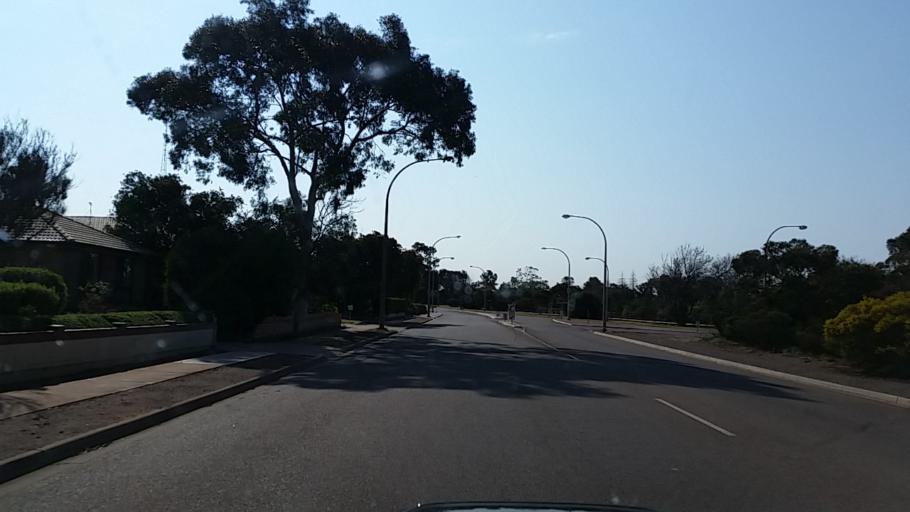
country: AU
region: South Australia
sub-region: Whyalla
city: Whyalla
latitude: -33.0308
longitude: 137.5826
